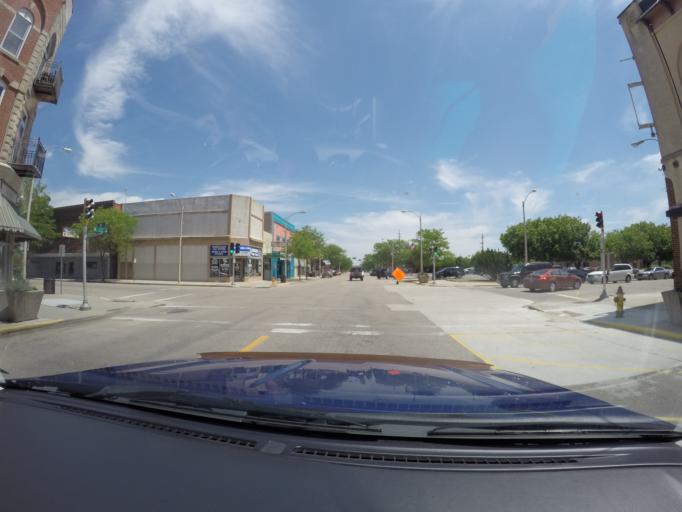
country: US
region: Nebraska
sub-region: Hall County
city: Grand Island
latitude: 40.9258
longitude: -98.3402
